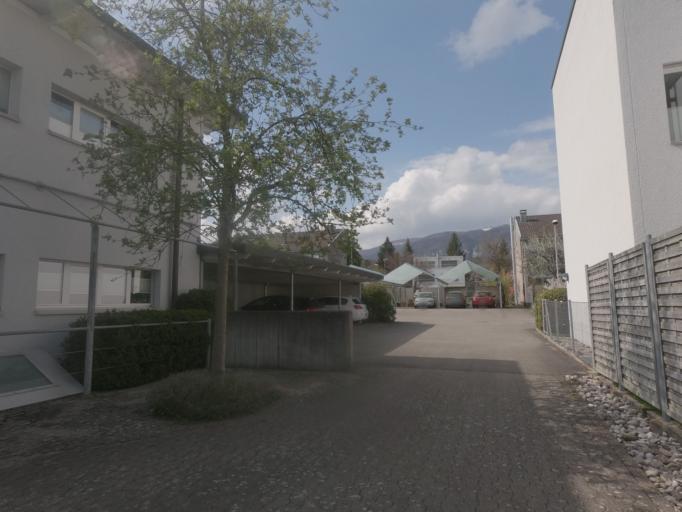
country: CH
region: Solothurn
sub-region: Bezirk Solothurn
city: Solothurn
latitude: 47.2161
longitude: 7.5461
